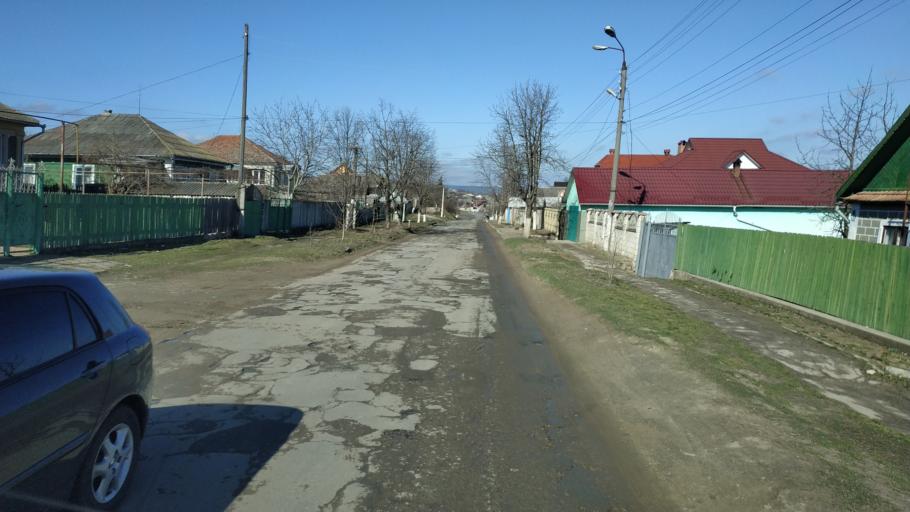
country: MD
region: Hincesti
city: Hincesti
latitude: 46.9687
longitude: 28.5909
